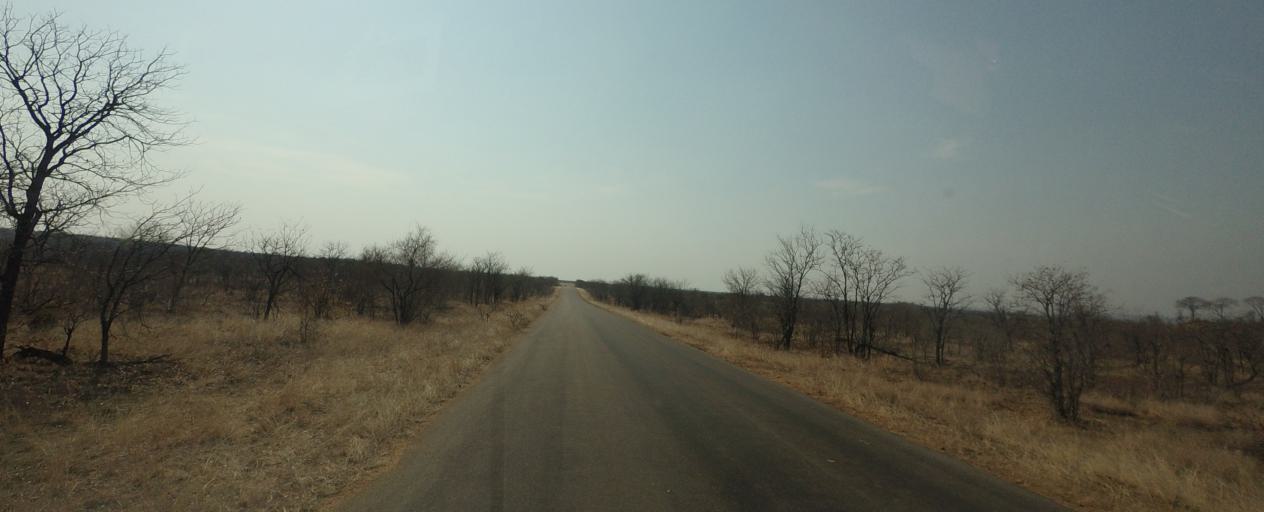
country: ZA
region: Limpopo
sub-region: Mopani District Municipality
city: Phalaborwa
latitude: -23.9529
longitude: 31.6210
